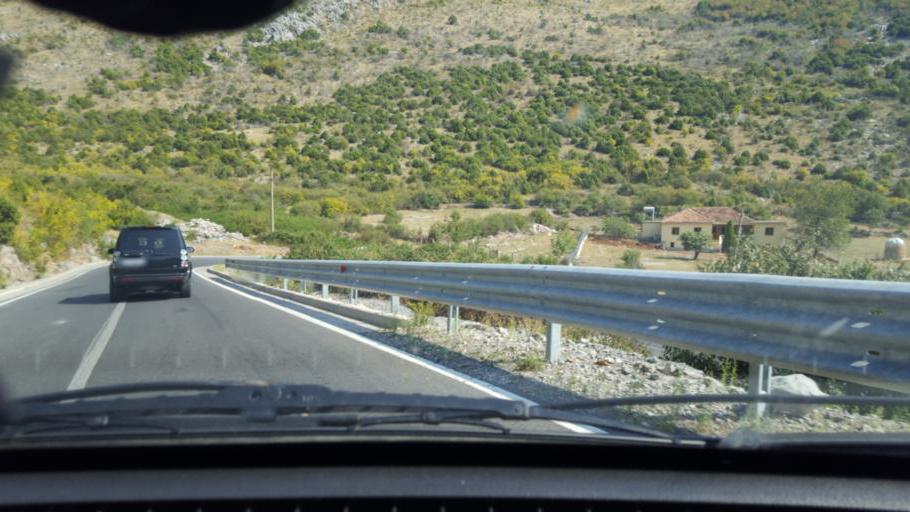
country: AL
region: Shkoder
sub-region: Rrethi i Malesia e Madhe
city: Hot
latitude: 42.3665
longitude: 19.4468
